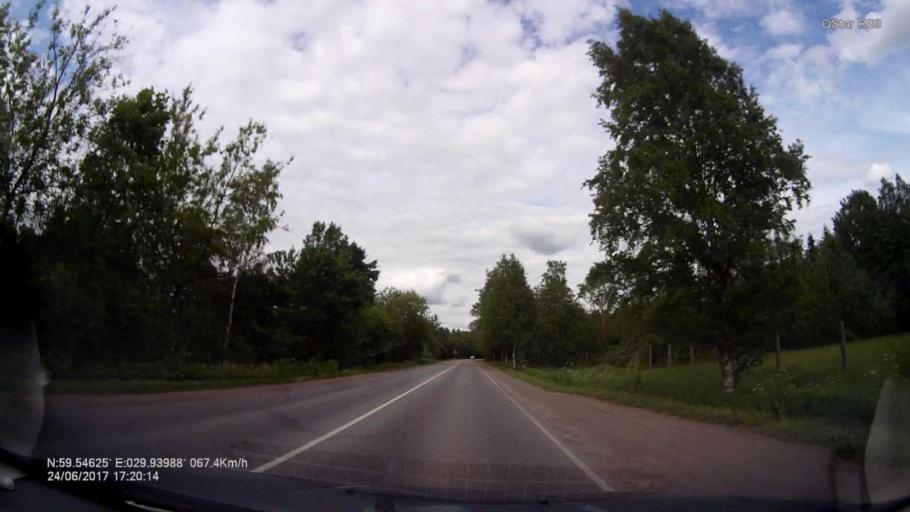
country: RU
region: Leningrad
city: Voyskovitsy
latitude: 59.5464
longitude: 29.9405
